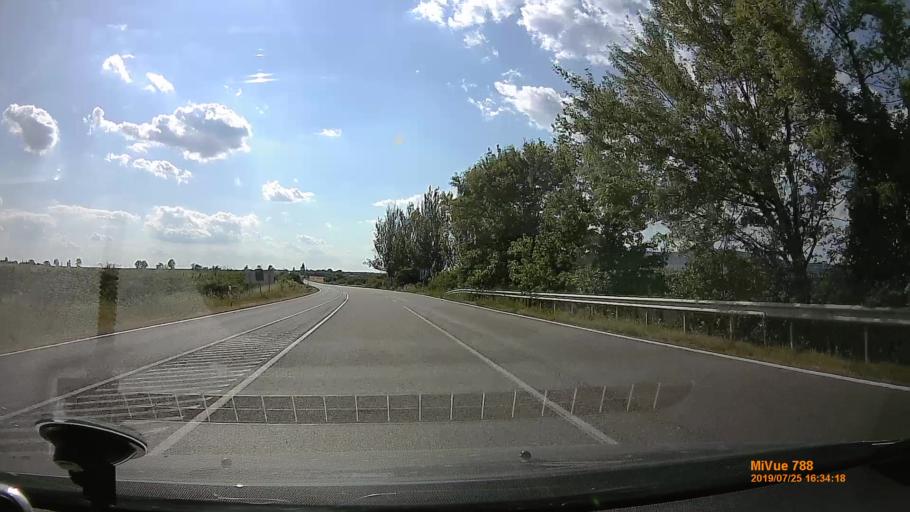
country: HU
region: Heves
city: Karacsond
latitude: 47.7670
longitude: 20.0266
